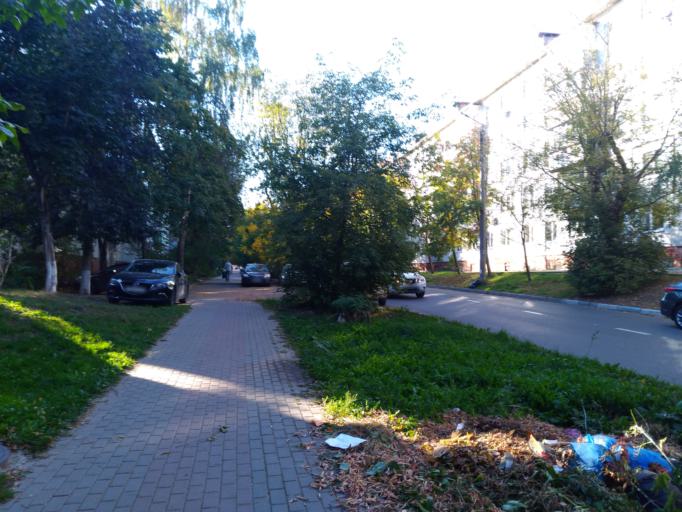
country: RU
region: Kaluga
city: Kaluga
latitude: 54.5180
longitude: 36.2705
